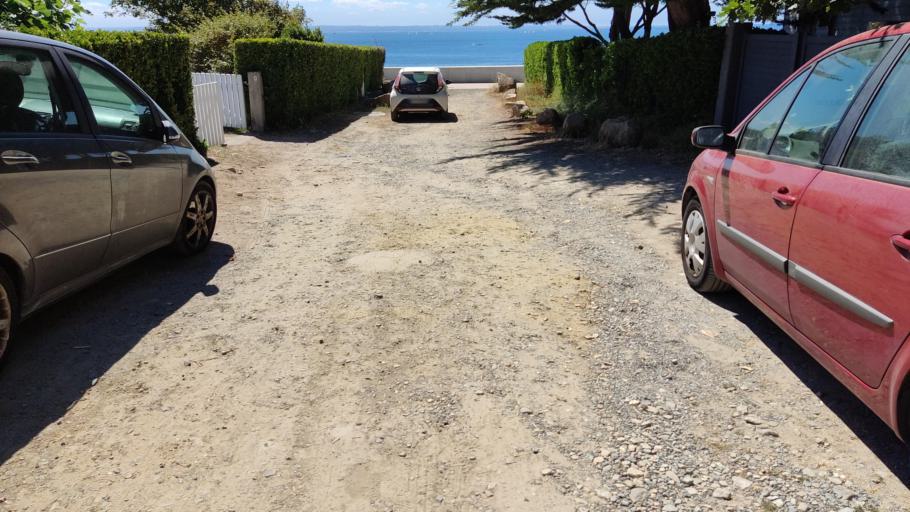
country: FR
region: Brittany
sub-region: Departement des Cotes-d'Armor
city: Trebeurden
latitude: 48.7662
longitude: -3.5790
